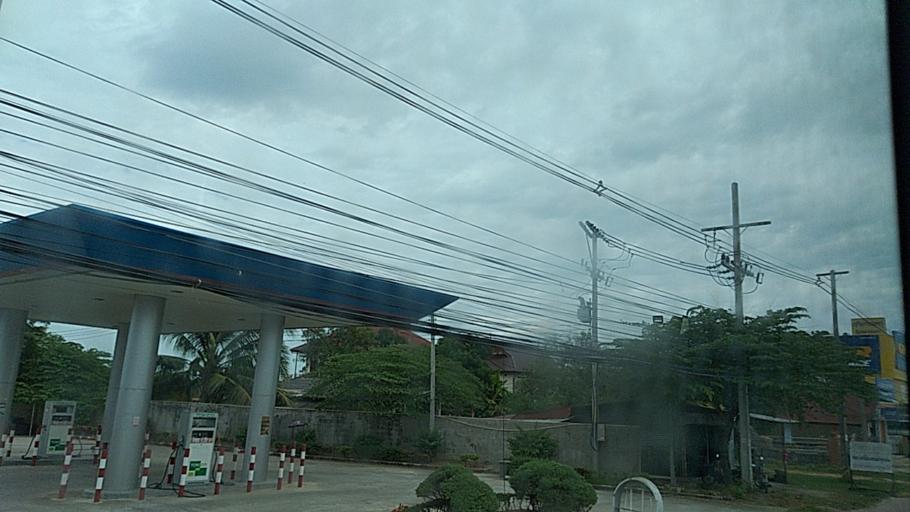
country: TH
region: Maha Sarakham
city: Maha Sarakham
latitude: 16.1685
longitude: 103.3256
